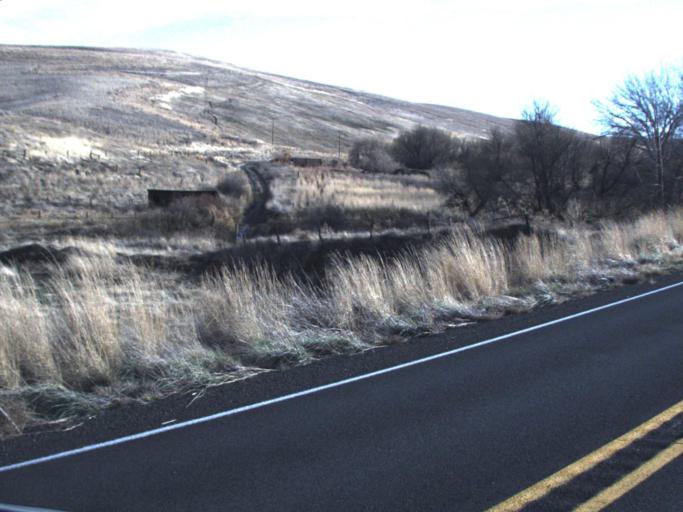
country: US
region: Washington
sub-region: Columbia County
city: Dayton
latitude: 46.4694
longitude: -117.9626
